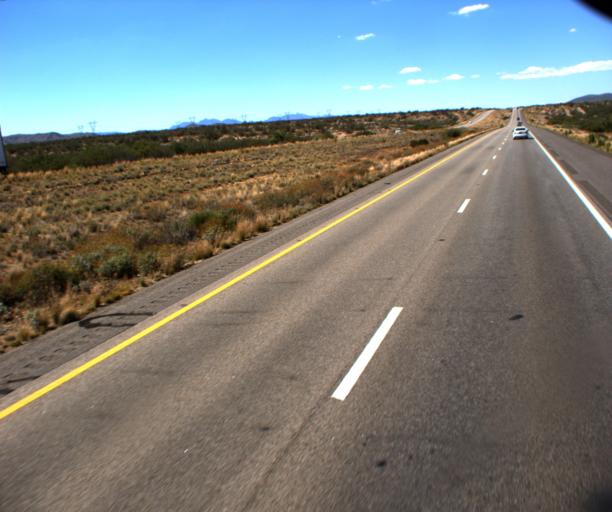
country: US
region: Arizona
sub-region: Mohave County
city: Kingman
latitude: 34.8543
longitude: -113.6389
